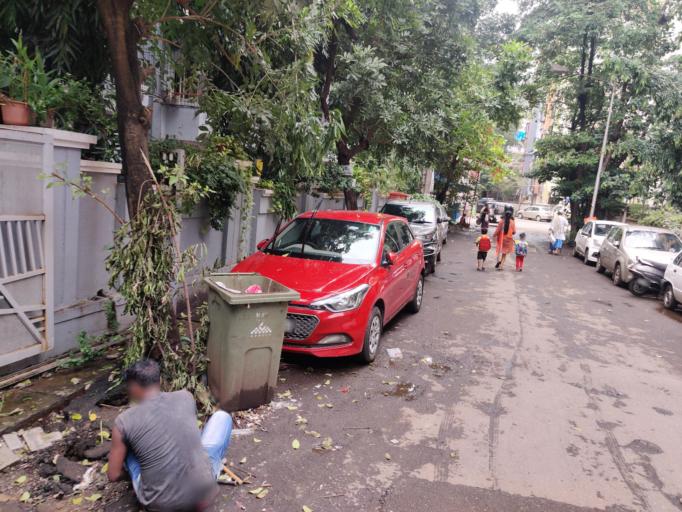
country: IN
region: Maharashtra
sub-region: Mumbai Suburban
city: Borivli
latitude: 19.2451
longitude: 72.8634
